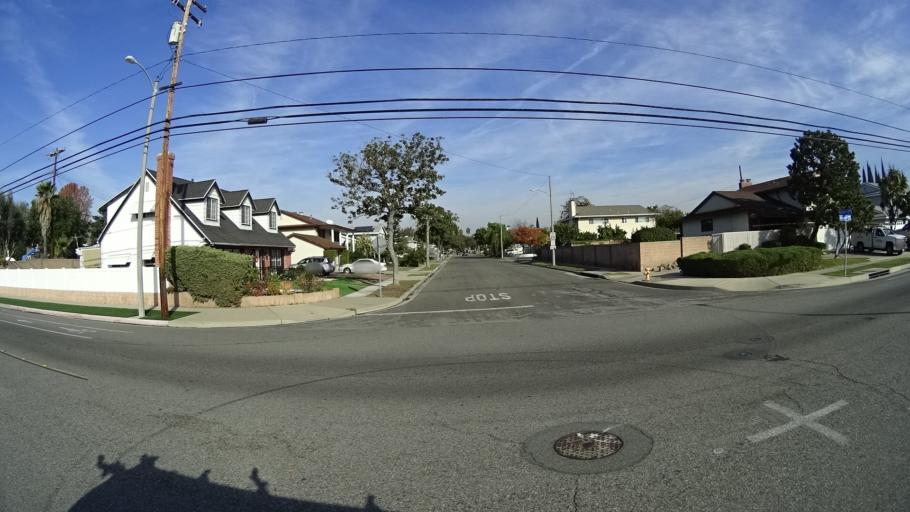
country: US
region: California
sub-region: Orange County
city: Garden Grove
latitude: 33.7958
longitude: -117.9344
